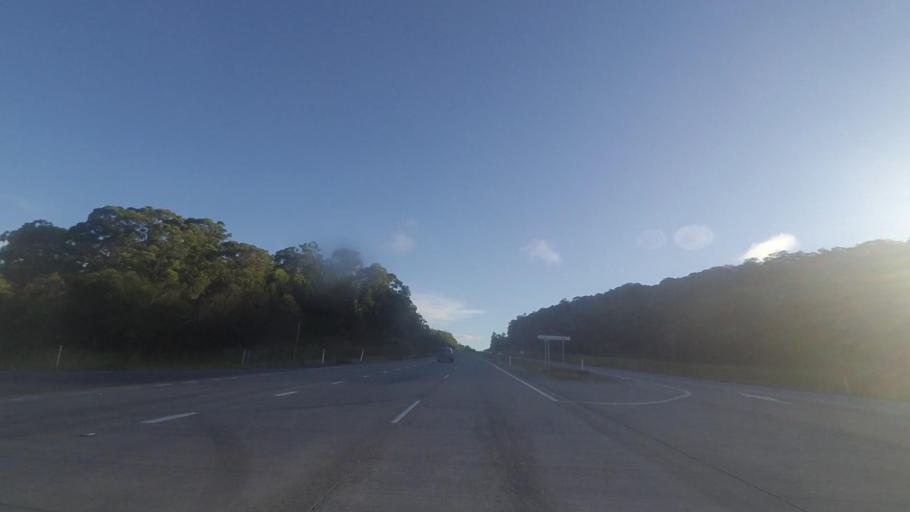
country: AU
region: New South Wales
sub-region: Great Lakes
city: Bulahdelah
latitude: -32.4684
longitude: 152.1960
